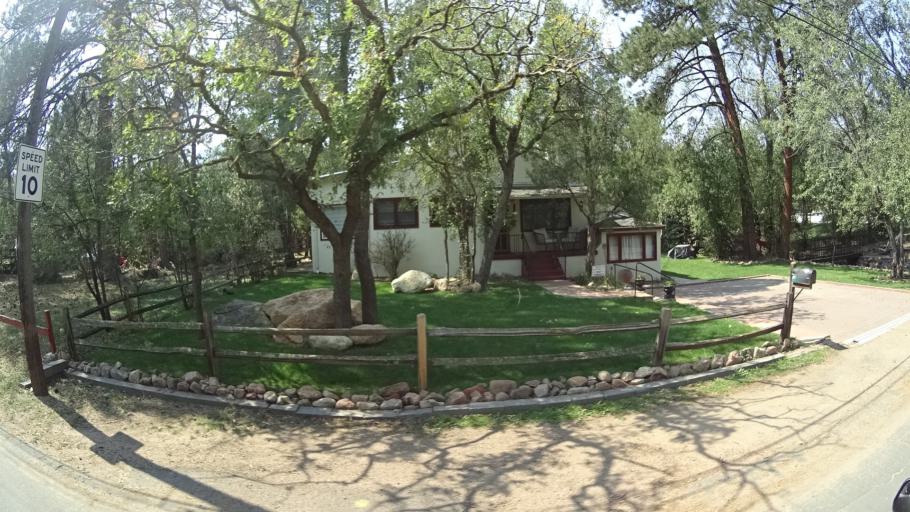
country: US
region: Colorado
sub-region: El Paso County
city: Colorado Springs
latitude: 38.7948
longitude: -104.8542
